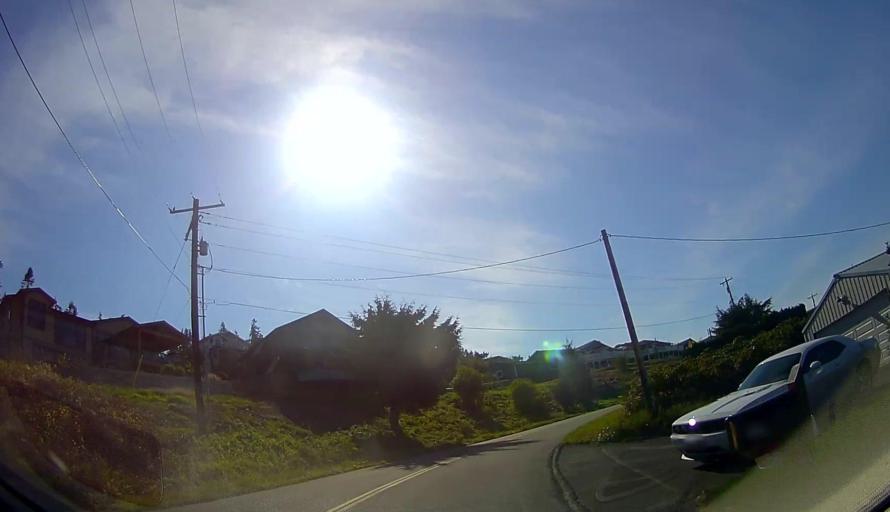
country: US
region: Washington
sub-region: Island County
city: Camano
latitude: 48.2458
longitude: -122.5271
